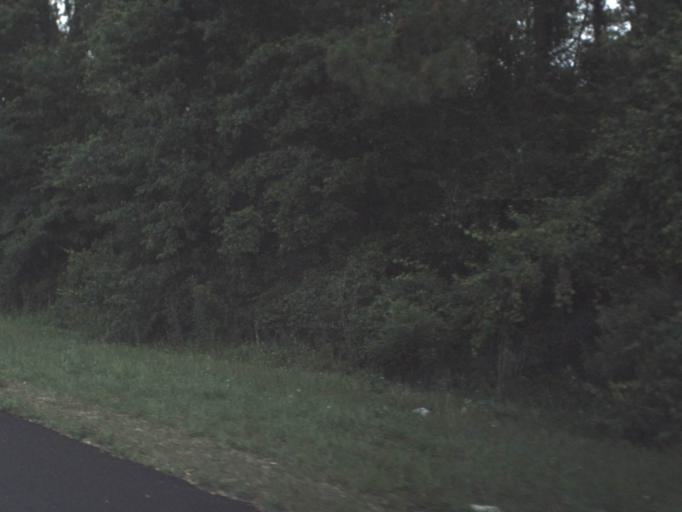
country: US
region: Florida
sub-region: Duval County
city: Baldwin
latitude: 30.1609
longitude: -82.0294
